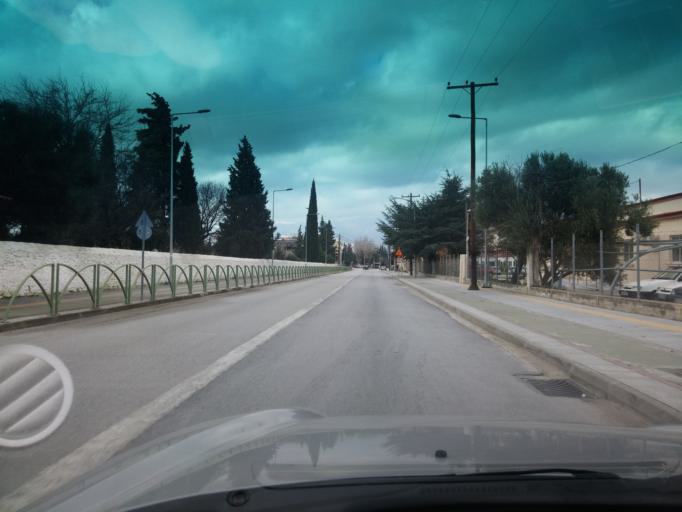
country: GR
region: East Macedonia and Thrace
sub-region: Nomos Rodopis
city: Komotini
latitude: 41.1228
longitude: 25.3974
